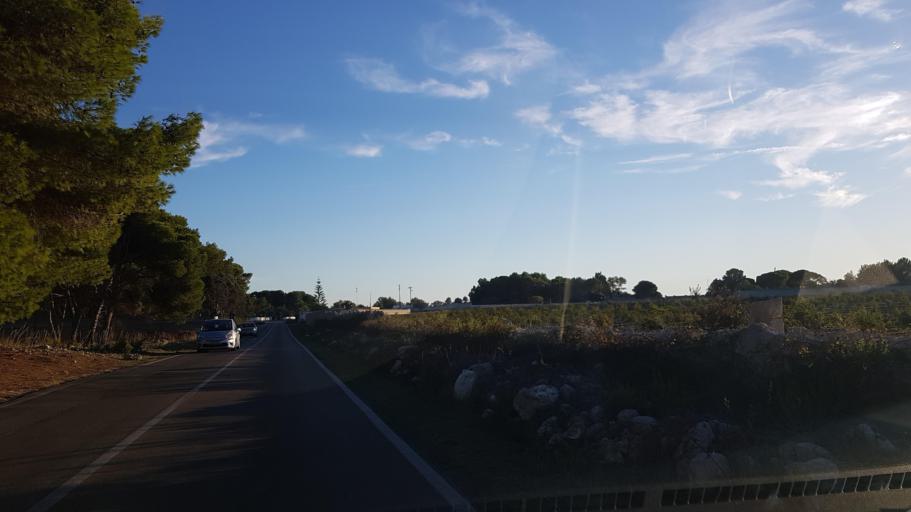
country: IT
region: Apulia
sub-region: Provincia di Lecce
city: Giorgilorio
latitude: 40.4020
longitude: 18.1966
